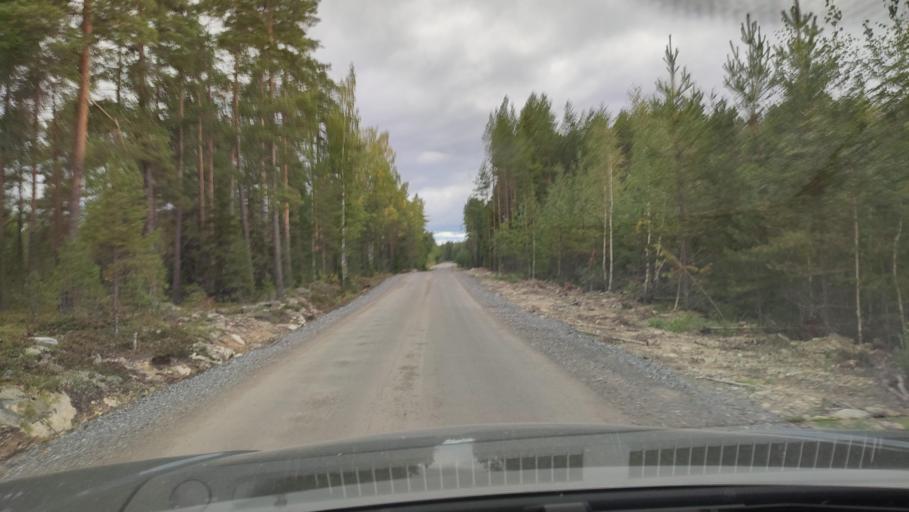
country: FI
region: Southern Ostrobothnia
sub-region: Suupohja
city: Karijoki
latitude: 62.1923
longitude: 21.5883
